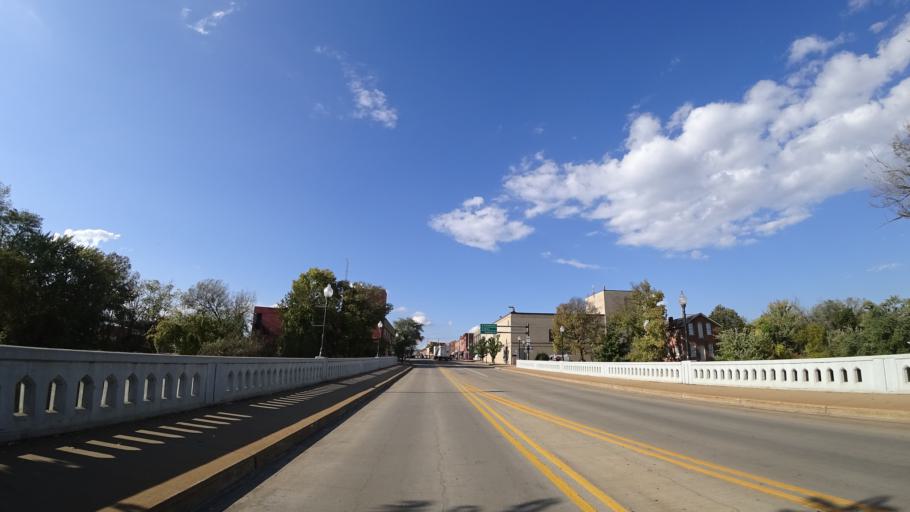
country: US
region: Michigan
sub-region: Saint Joseph County
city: Three Rivers
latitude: 41.9430
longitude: -85.6320
